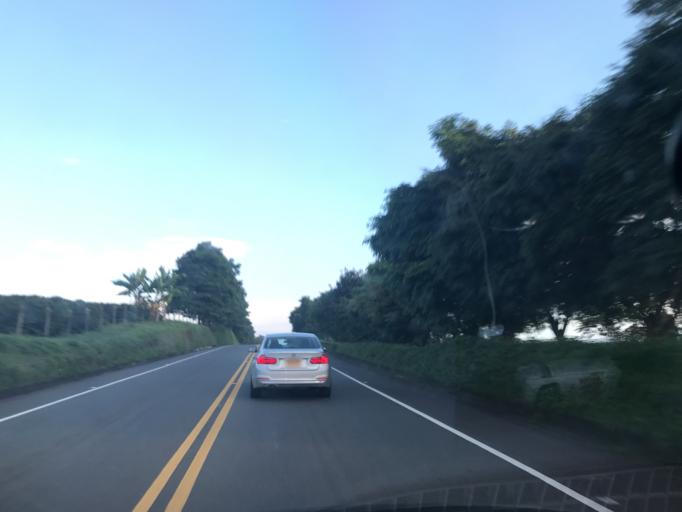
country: CO
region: Risaralda
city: Pereira
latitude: 4.7506
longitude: -75.6949
